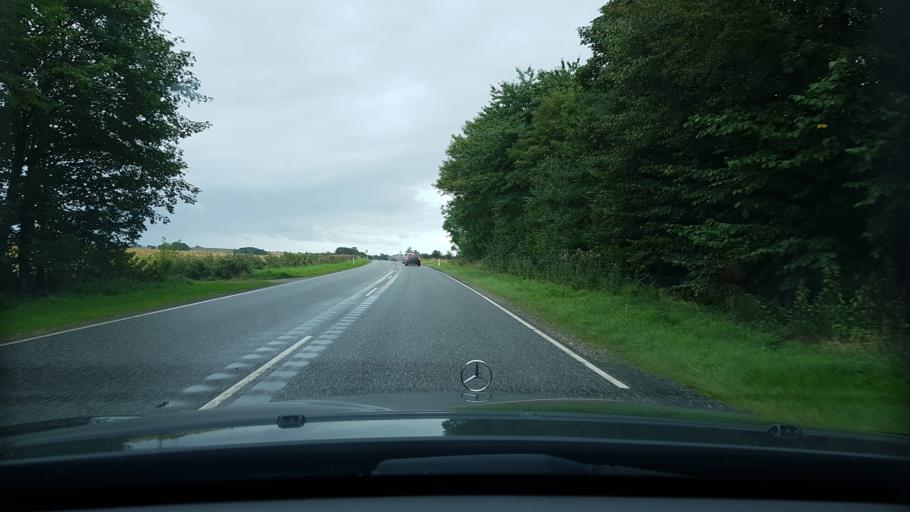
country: DK
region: Central Jutland
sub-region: Randers Kommune
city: Spentrup
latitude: 56.5398
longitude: 10.0952
